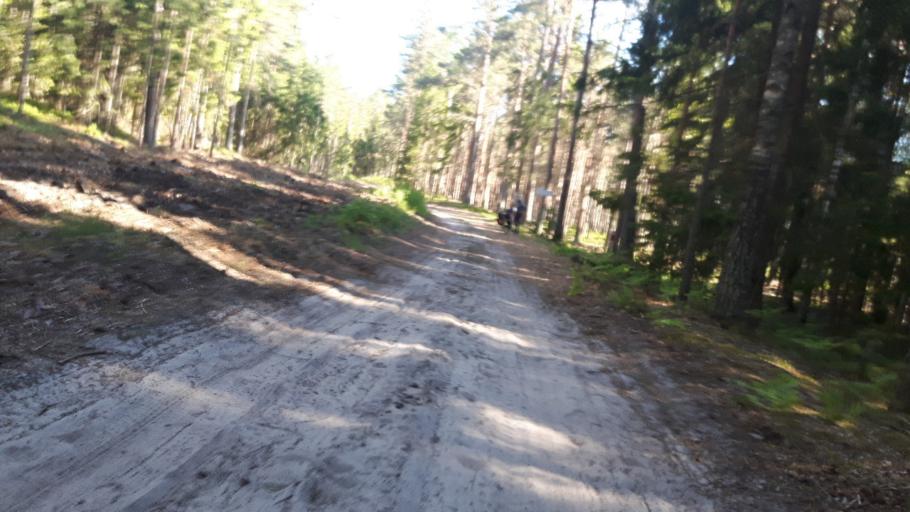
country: LV
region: Salacgrivas
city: Salacgriva
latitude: 57.7177
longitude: 24.3478
